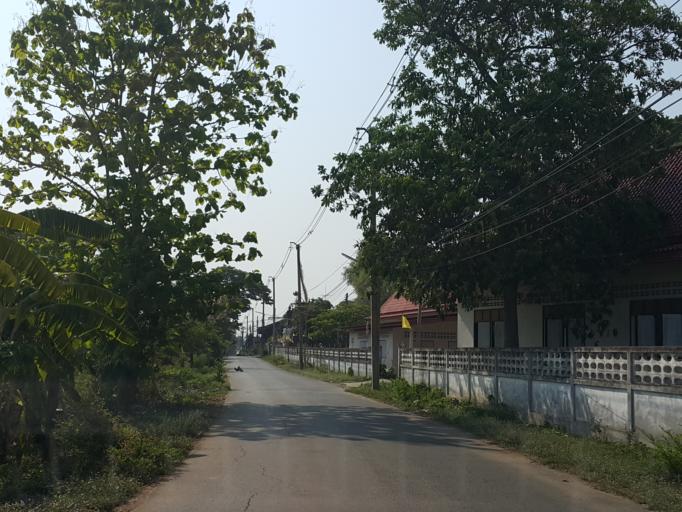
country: TH
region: Kanchanaburi
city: Sai Yok
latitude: 14.1208
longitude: 99.1365
